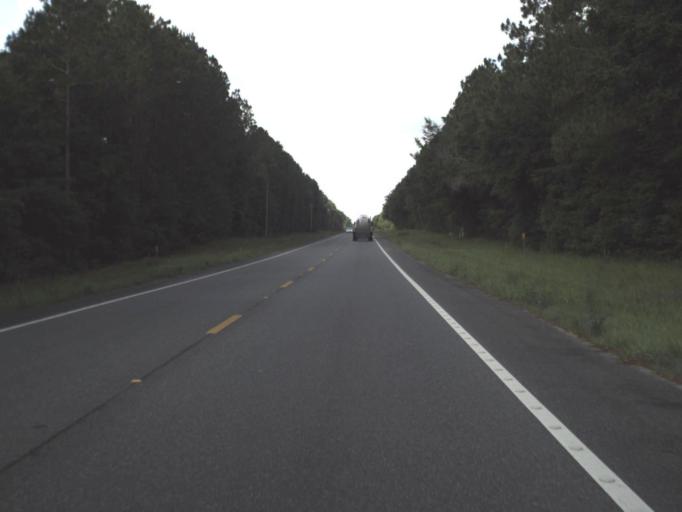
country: US
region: Florida
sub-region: Suwannee County
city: Wellborn
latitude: 30.0244
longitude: -82.8314
